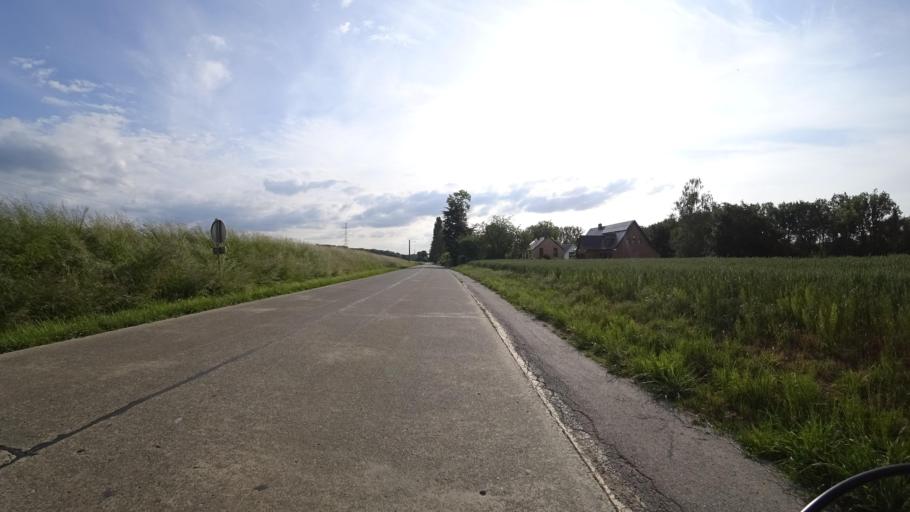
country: BE
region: Wallonia
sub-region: Province de Namur
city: Namur
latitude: 50.5130
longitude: 4.8290
